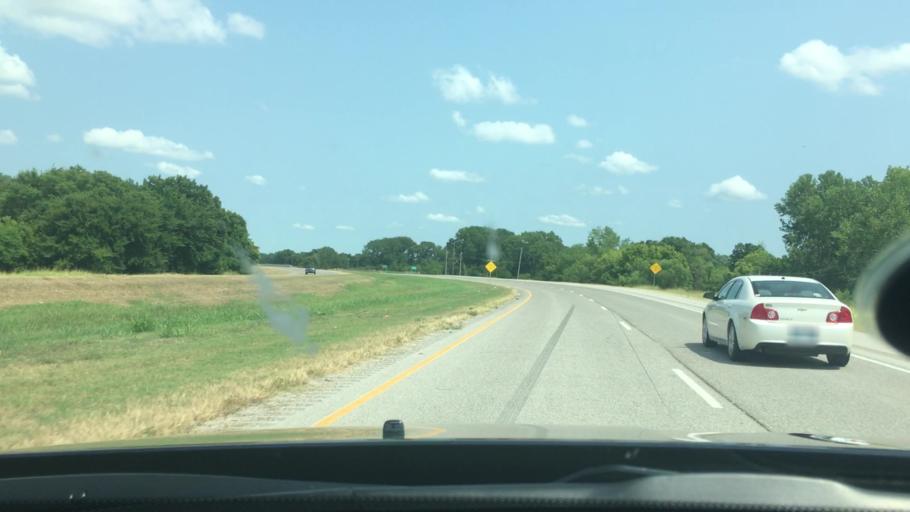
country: US
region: Oklahoma
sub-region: Murray County
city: Davis
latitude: 34.5058
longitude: -97.1467
